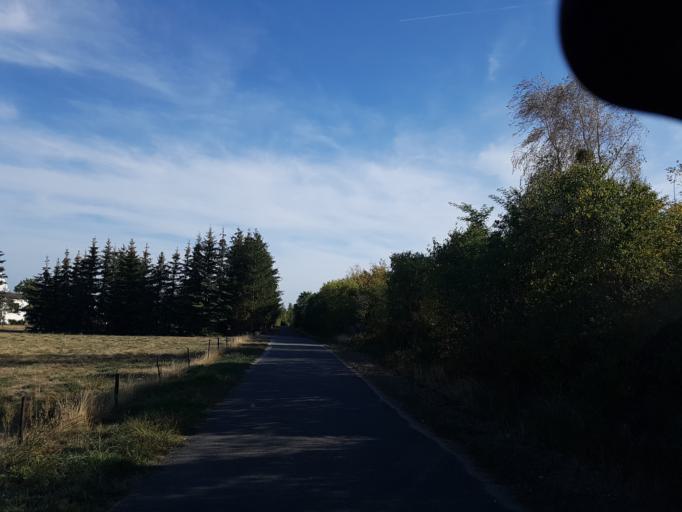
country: DE
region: Saxony-Anhalt
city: Jessen
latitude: 51.8007
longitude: 12.9931
